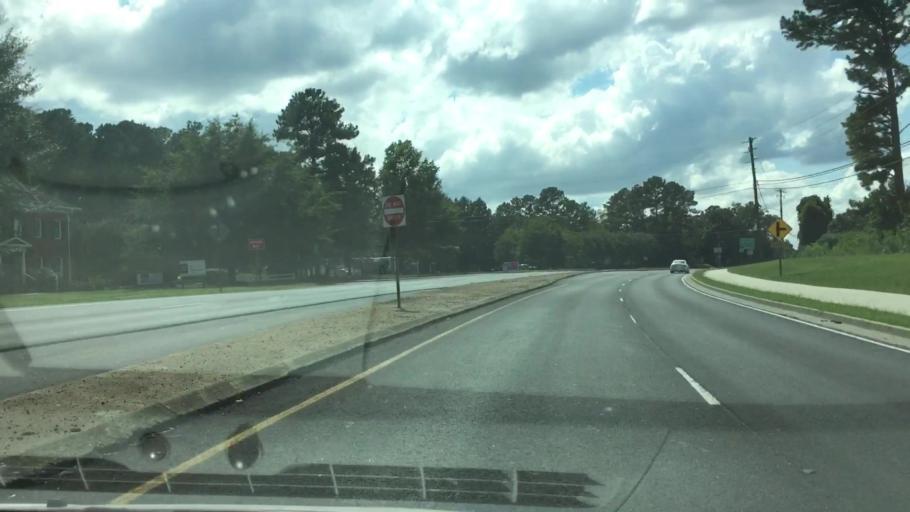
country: US
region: Georgia
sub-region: Fayette County
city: Fayetteville
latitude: 33.4514
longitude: -84.4334
